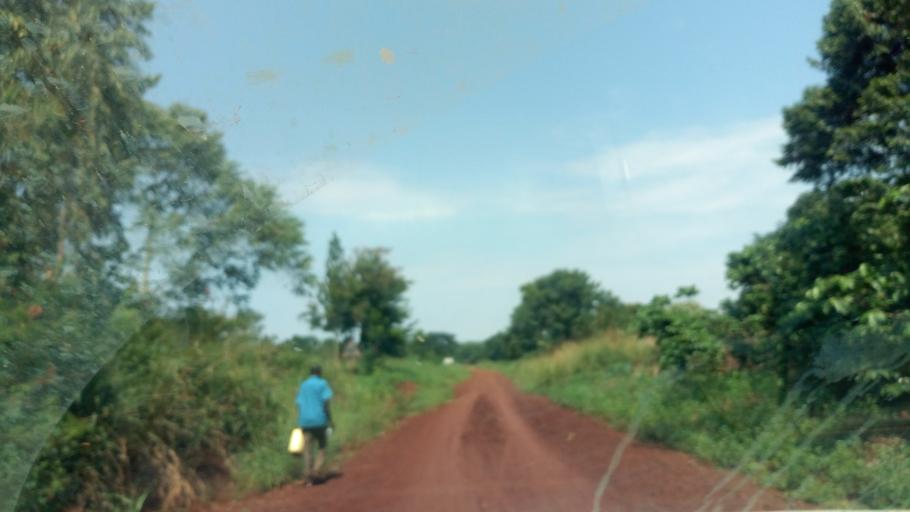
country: UG
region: Western Region
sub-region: Masindi District
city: Masindi
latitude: 1.6695
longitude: 31.8228
